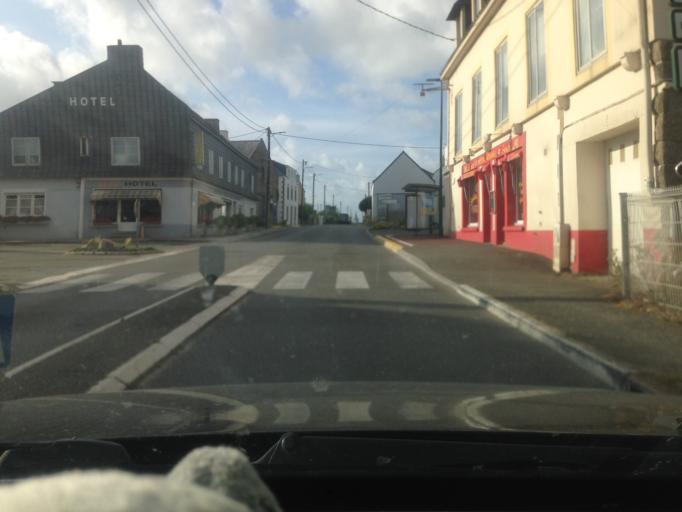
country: FR
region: Brittany
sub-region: Departement du Morbihan
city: Plouharnel
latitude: 47.6042
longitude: -3.1192
